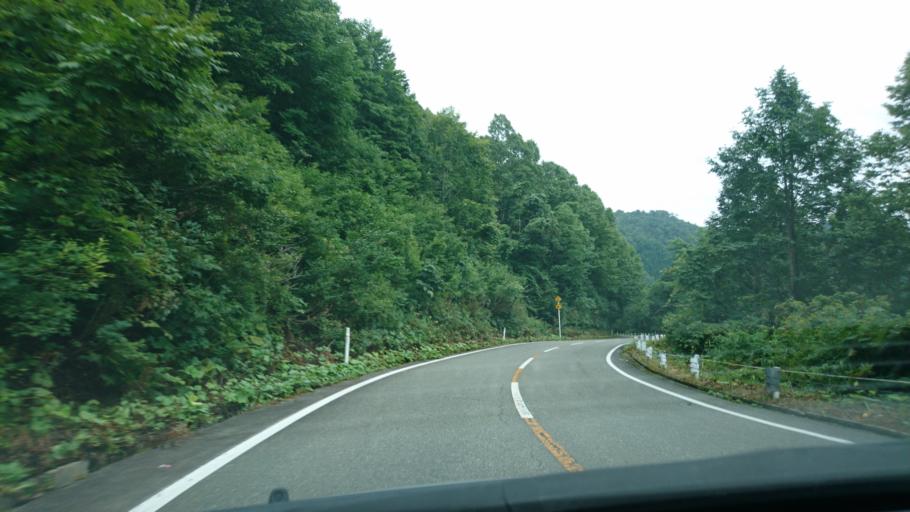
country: JP
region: Akita
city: Yuzawa
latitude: 38.9780
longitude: 140.7207
